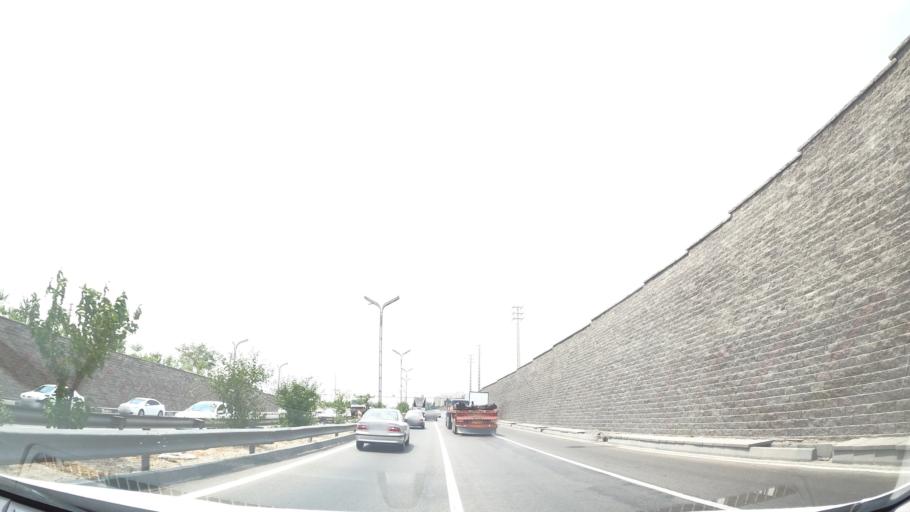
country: IR
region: Tehran
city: Shahr-e Qods
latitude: 35.7035
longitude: 51.1835
